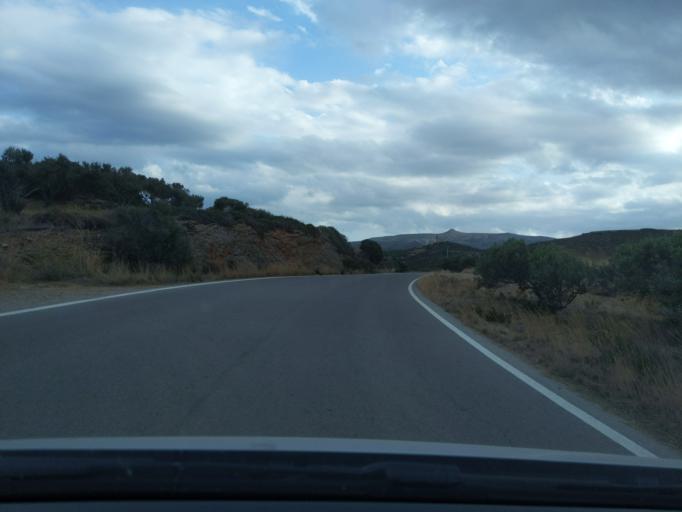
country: GR
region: Crete
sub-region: Nomos Lasithiou
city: Palekastro
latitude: 35.2280
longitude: 26.2559
